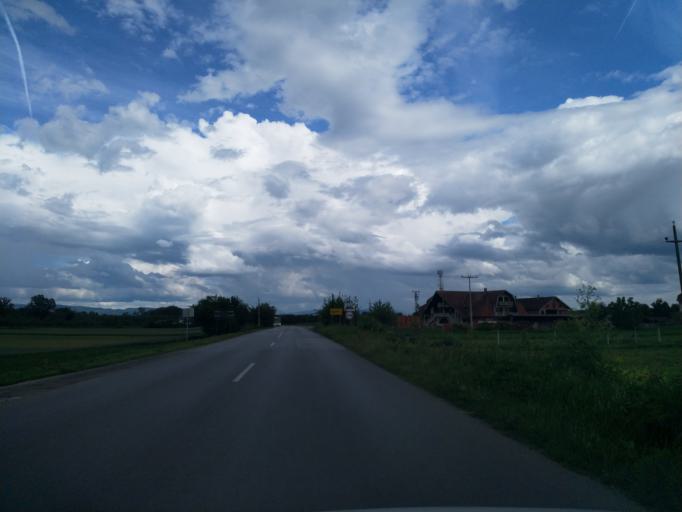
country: RS
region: Central Serbia
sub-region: Pomoravski Okrug
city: Cuprija
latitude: 43.9456
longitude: 21.3402
